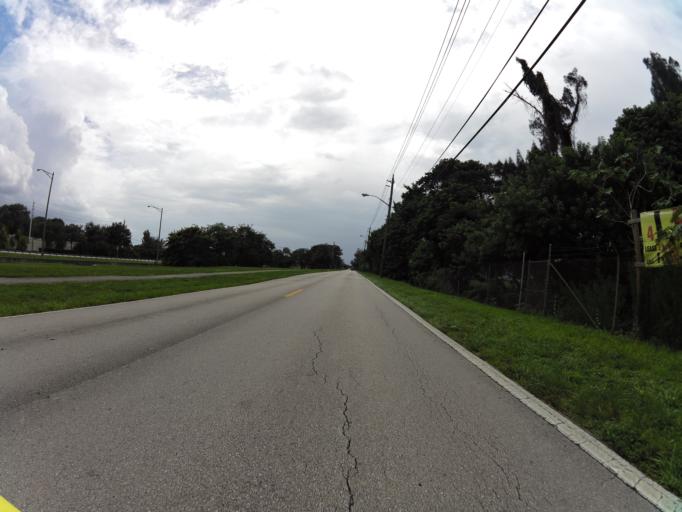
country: US
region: Florida
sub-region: Broward County
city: Cooper City
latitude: 26.0650
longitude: -80.2721
